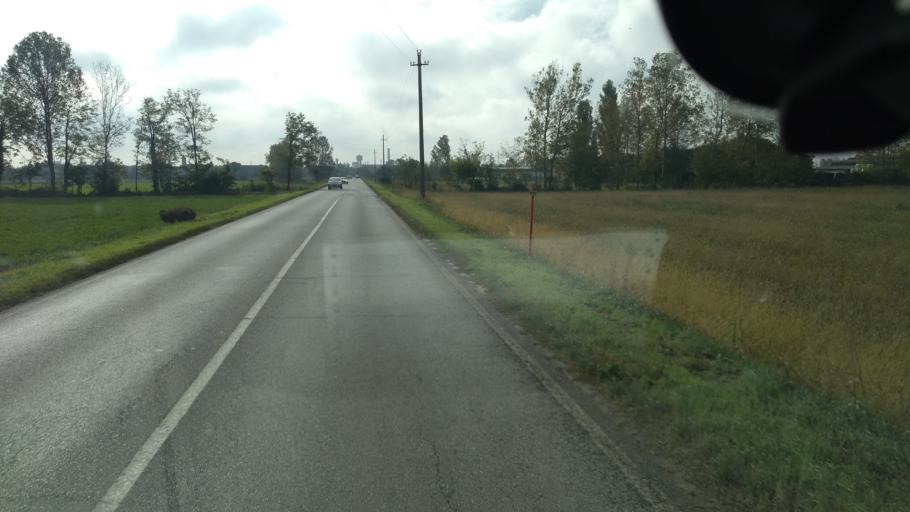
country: IT
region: Lombardy
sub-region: Provincia di Bergamo
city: Vidalengo
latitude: 45.5298
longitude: 9.6389
